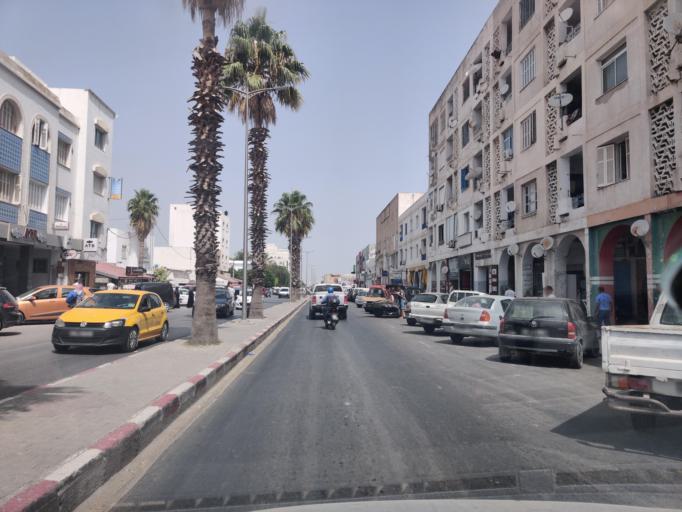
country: TN
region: Nabul
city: Bu `Urqub
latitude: 36.5997
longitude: 10.4982
